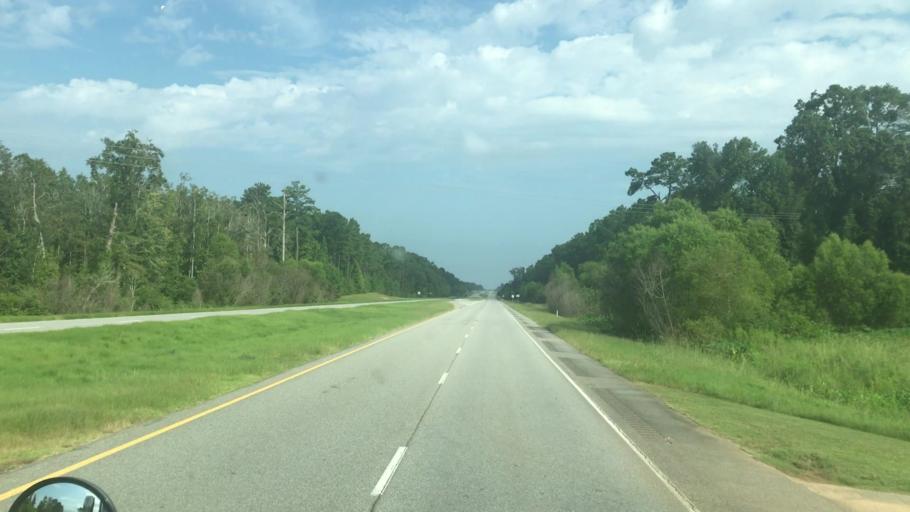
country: US
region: Georgia
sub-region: Early County
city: Blakely
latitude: 31.2944
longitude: -84.8529
